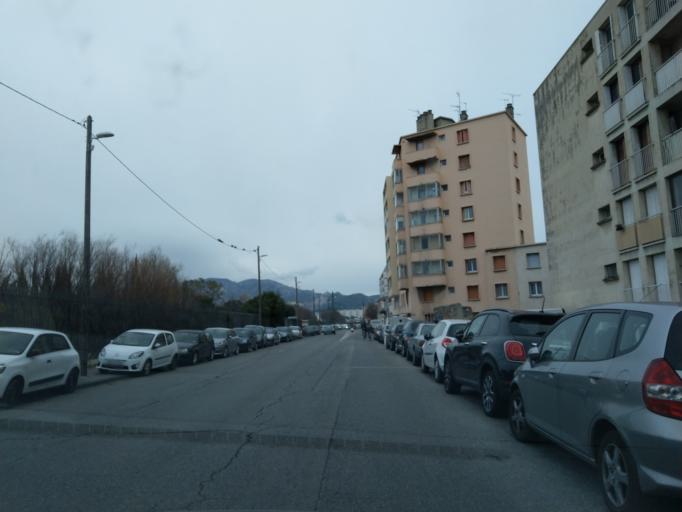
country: FR
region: Provence-Alpes-Cote d'Azur
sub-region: Departement des Bouches-du-Rhone
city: Marseille 08
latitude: 43.2802
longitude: 5.3941
